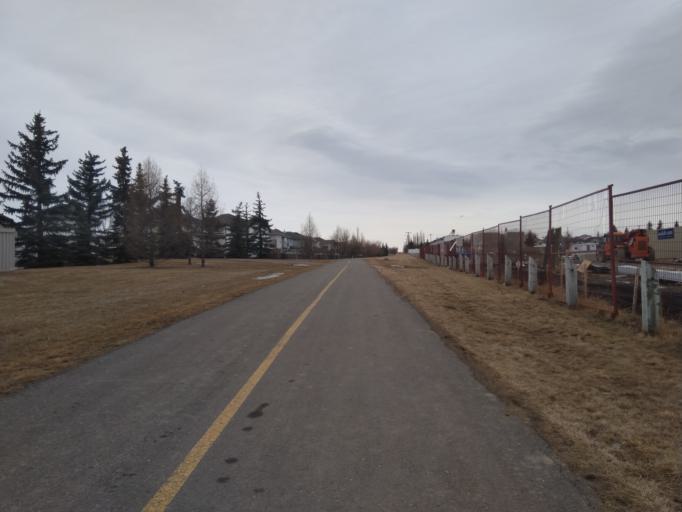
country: CA
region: Alberta
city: Calgary
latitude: 51.1572
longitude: -114.0480
